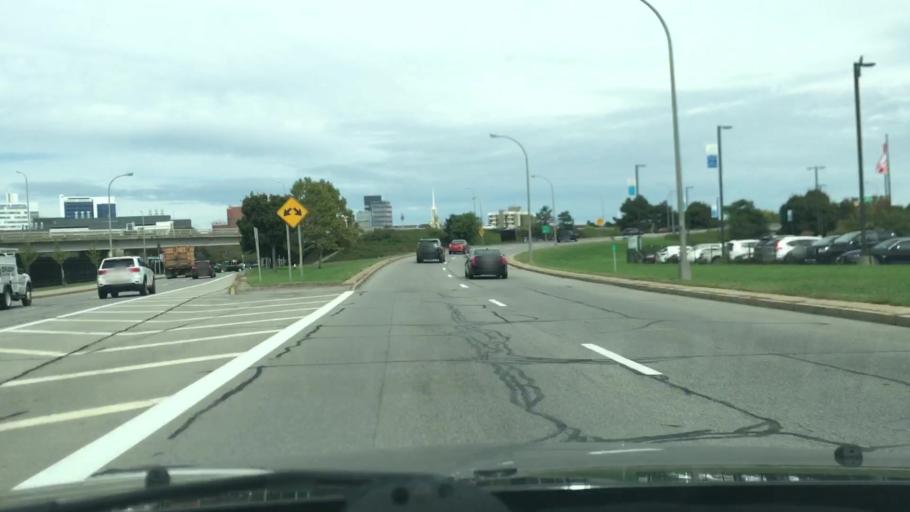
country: US
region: New York
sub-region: Erie County
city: Buffalo
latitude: 42.8917
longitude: -78.8672
